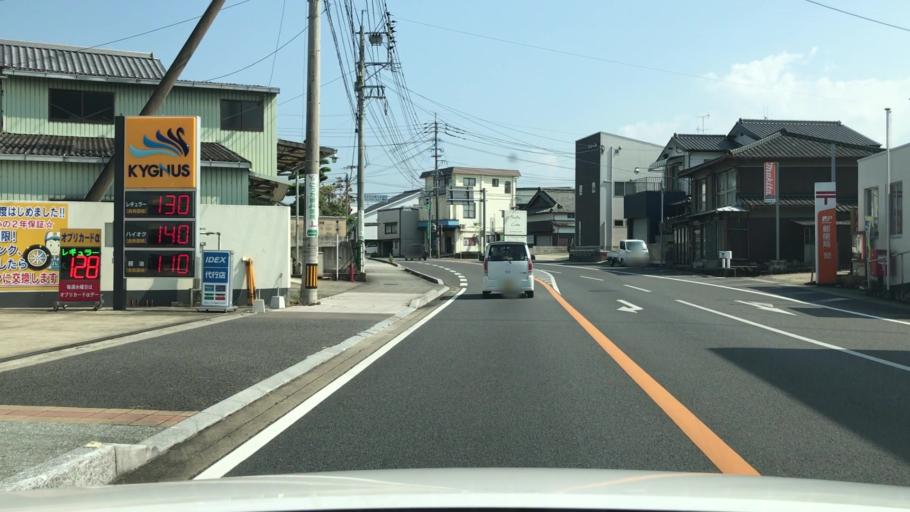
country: JP
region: Saga Prefecture
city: Kashima
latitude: 33.1273
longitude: 130.0593
